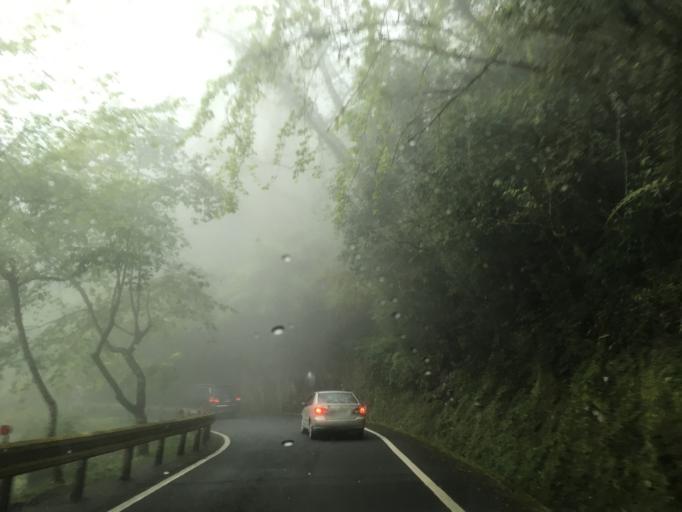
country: TW
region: Taiwan
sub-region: Hualien
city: Hualian
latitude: 24.1858
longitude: 121.4168
